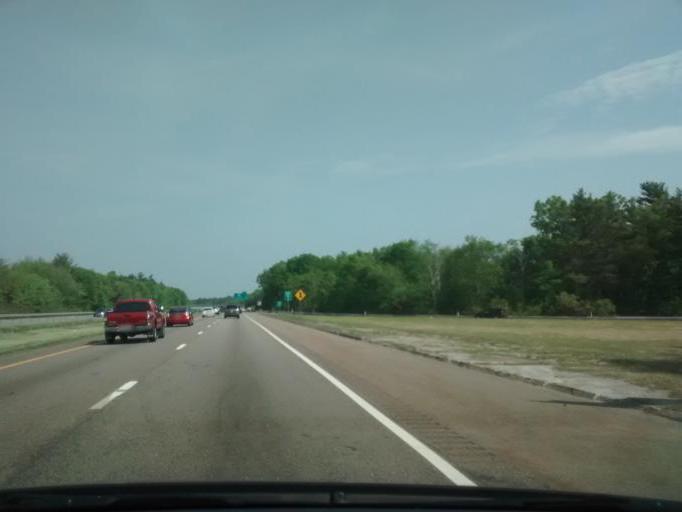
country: US
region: Massachusetts
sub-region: Plymouth County
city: Middleborough Center
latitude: 41.9018
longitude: -70.9639
